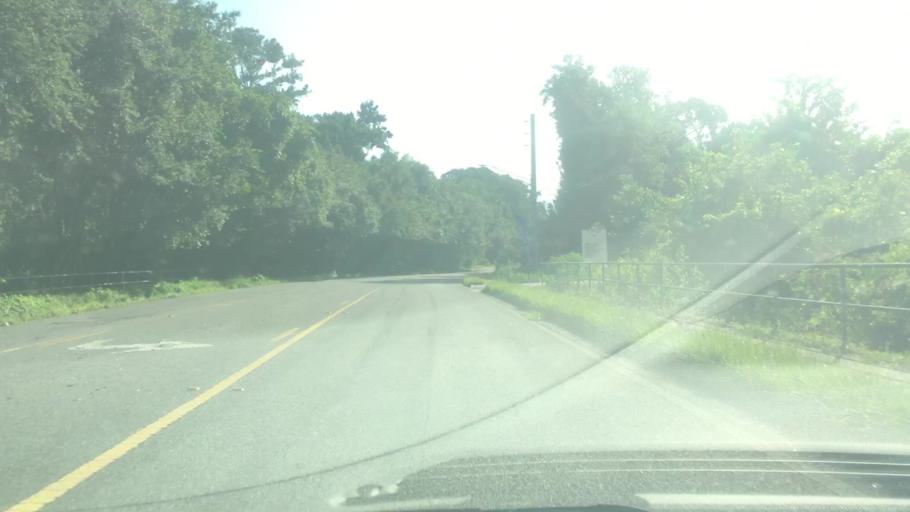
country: US
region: Florida
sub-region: Duval County
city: Jacksonville
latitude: 30.2919
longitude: -81.6143
